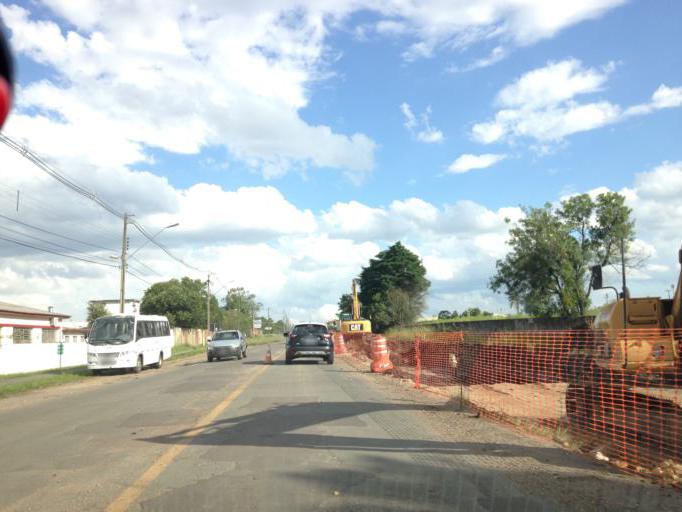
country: BR
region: Parana
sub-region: Pinhais
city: Pinhais
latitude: -25.4192
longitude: -49.2180
